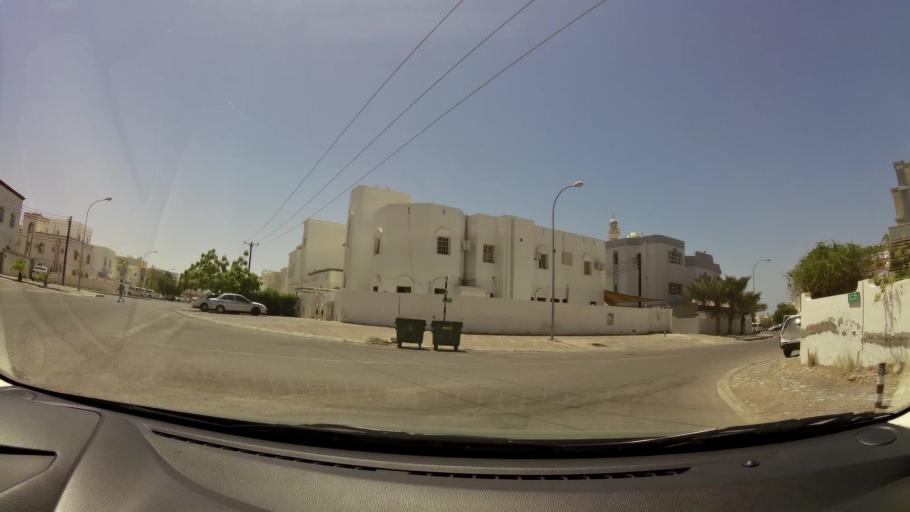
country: OM
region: Muhafazat Masqat
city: Bawshar
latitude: 23.5950
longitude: 58.3729
